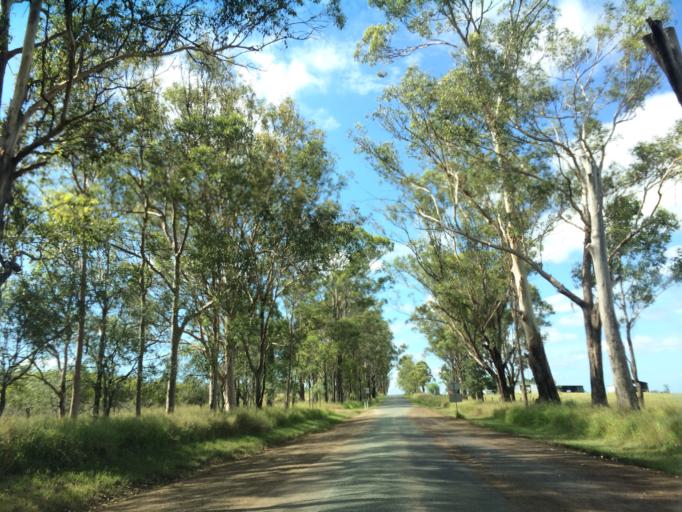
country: AU
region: Queensland
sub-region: Logan
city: Cedar Vale
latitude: -27.8829
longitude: 152.9719
